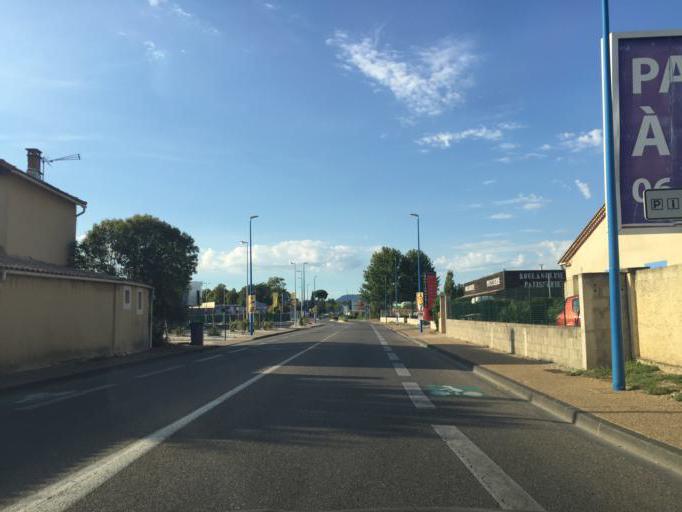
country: FR
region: Provence-Alpes-Cote d'Azur
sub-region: Departement du Vaucluse
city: Carpentras
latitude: 44.0360
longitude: 5.0509
